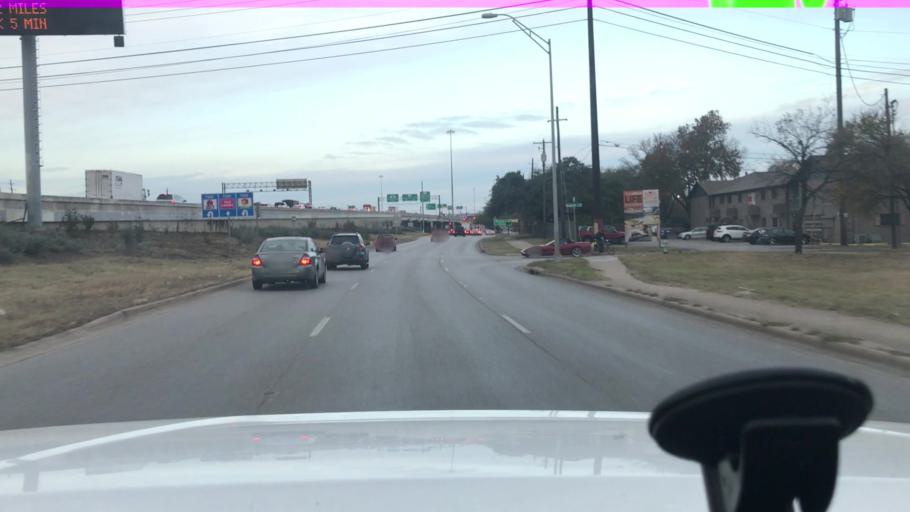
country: US
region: Texas
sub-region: Travis County
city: Rollingwood
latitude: 30.2291
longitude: -97.7853
